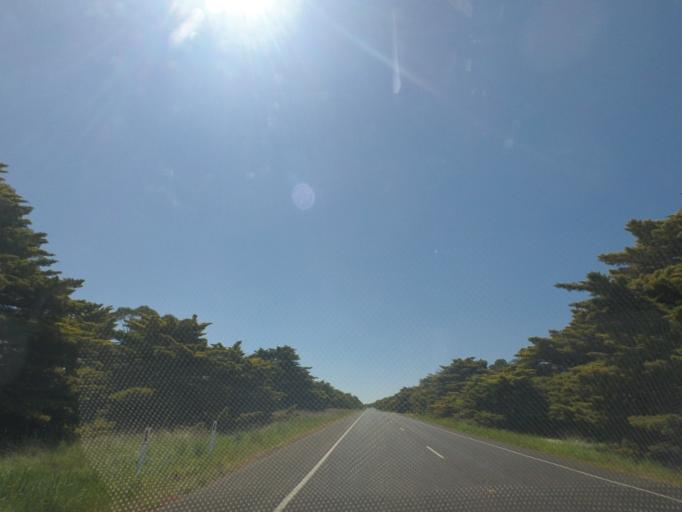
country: AU
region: Victoria
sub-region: Hume
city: Sunbury
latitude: -37.4453
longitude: 144.7445
